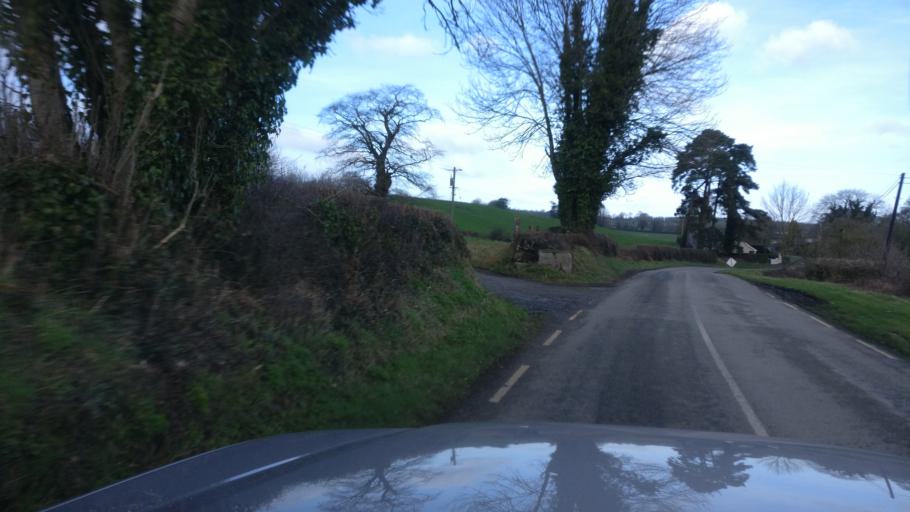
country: IE
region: Leinster
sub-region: Kilkenny
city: Castlecomer
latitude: 52.8208
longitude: -7.2123
